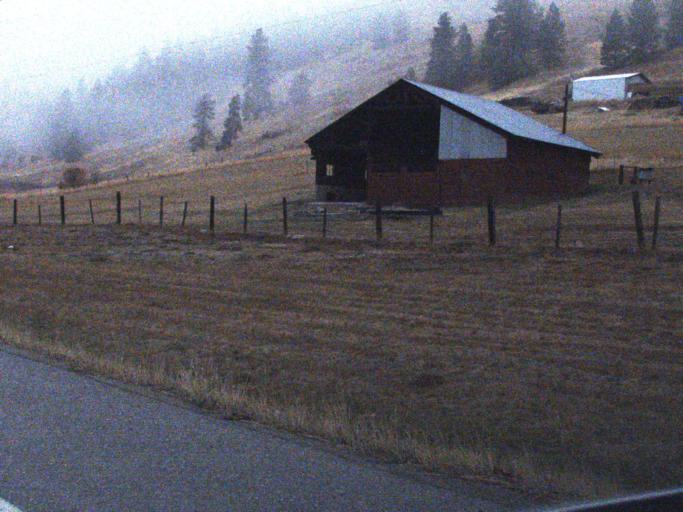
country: US
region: Washington
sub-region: Stevens County
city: Kettle Falls
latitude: 48.6114
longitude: -118.0401
